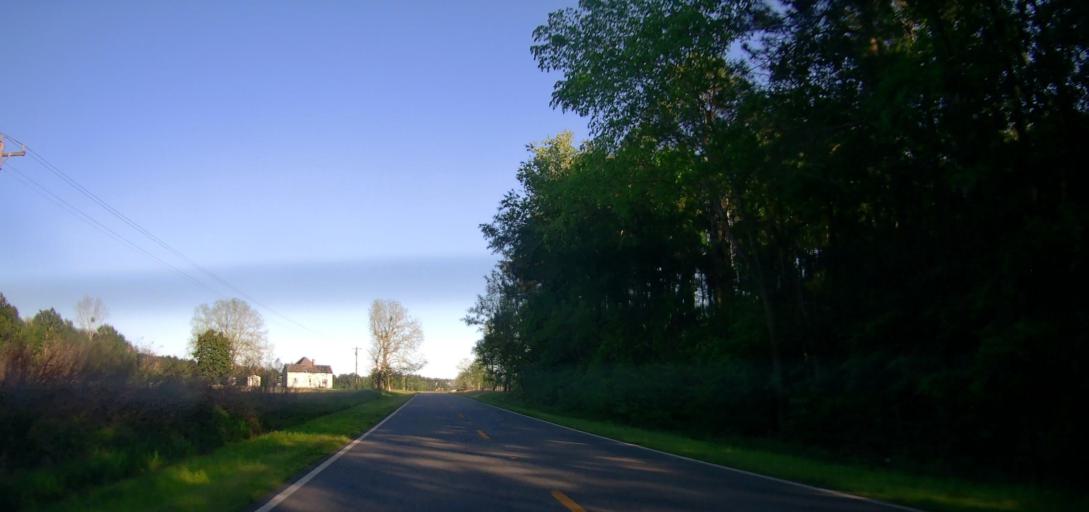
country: US
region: Georgia
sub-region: Ben Hill County
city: Fitzgerald
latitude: 31.6805
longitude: -83.2001
